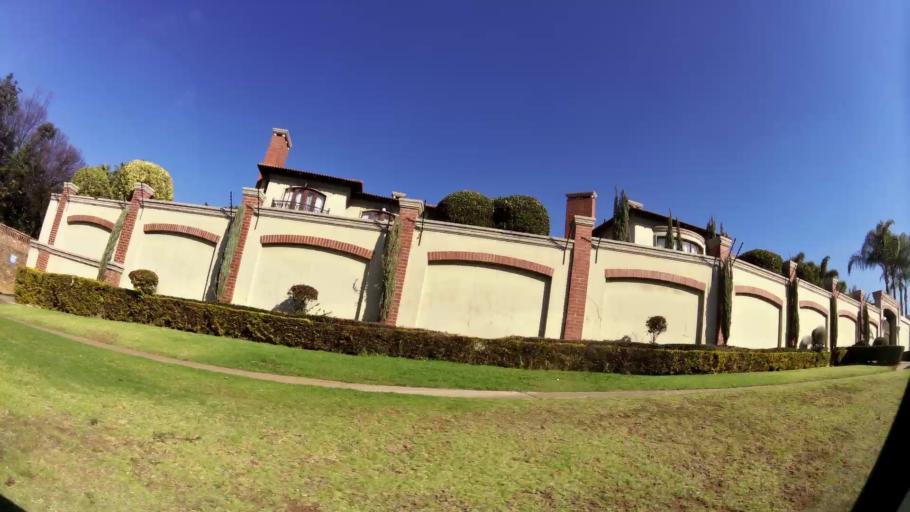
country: ZA
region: Gauteng
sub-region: City of Tshwane Metropolitan Municipality
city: Pretoria
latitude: -25.7881
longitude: 28.2495
